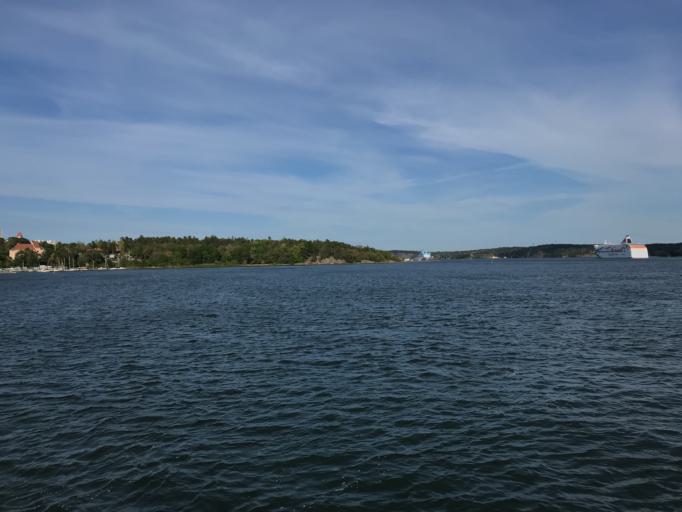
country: SE
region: Stockholm
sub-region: Nacka Kommun
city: Nacka
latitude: 59.3398
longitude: 18.1526
